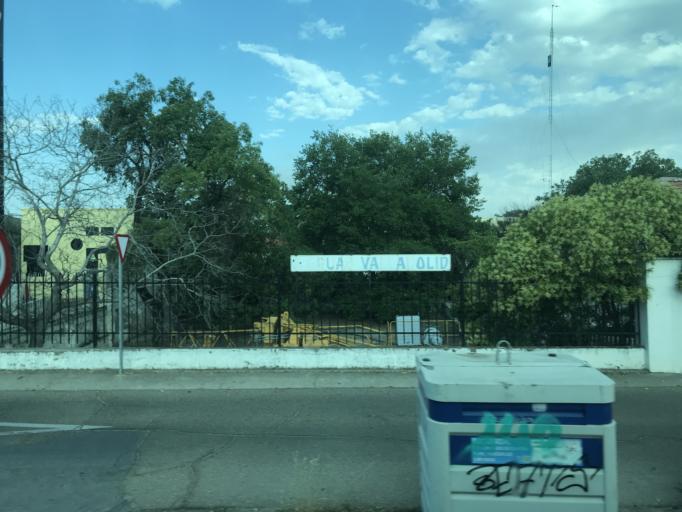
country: ES
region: Castille and Leon
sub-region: Provincia de Valladolid
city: Valladolid
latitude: 41.6190
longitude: -4.7263
